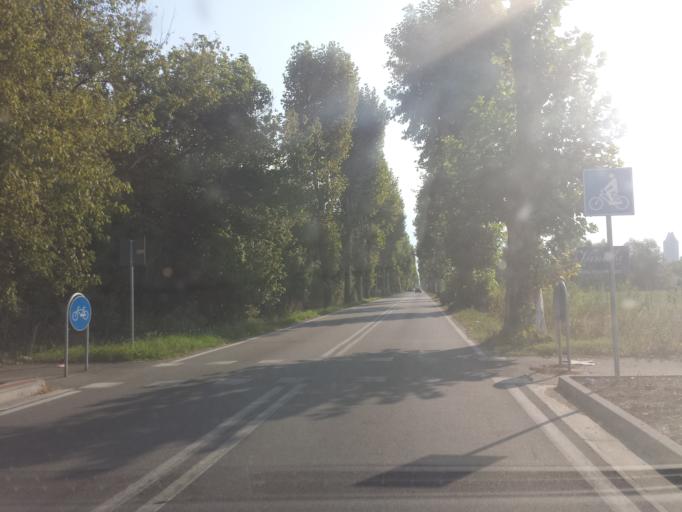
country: IT
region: Veneto
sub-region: Provincia di Venezia
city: Lido di Iesolo
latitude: 45.4976
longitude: 12.6027
